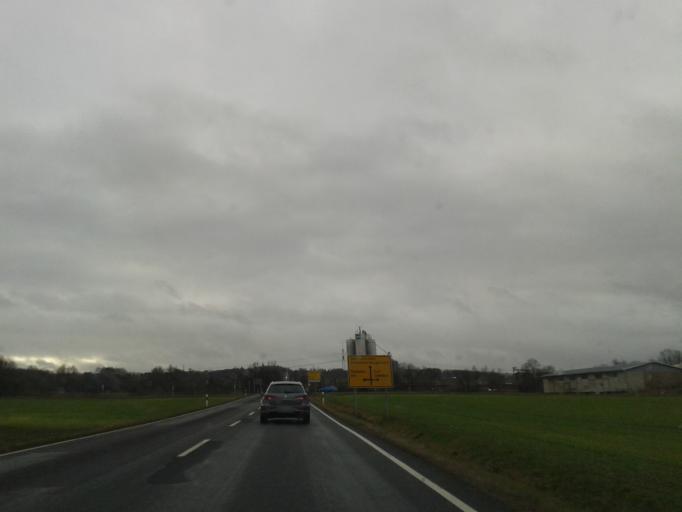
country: DE
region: Saxony
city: Grossschweidnitz
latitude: 51.0565
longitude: 14.6419
